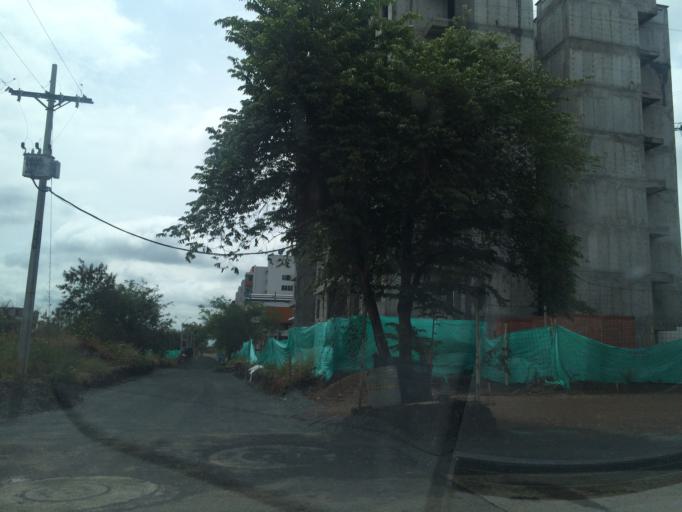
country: CO
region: Valle del Cauca
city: Cali
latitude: 3.3571
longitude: -76.5195
